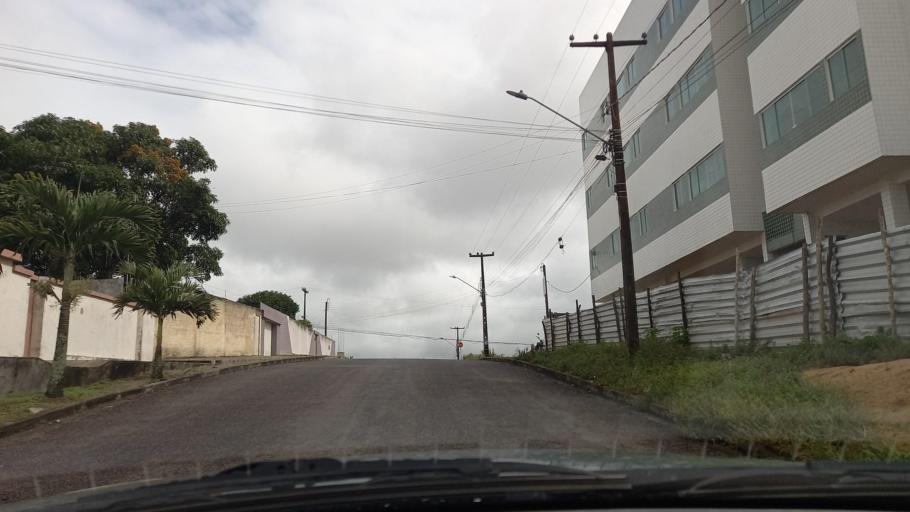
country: BR
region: Pernambuco
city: Garanhuns
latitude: -8.9028
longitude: -36.4909
